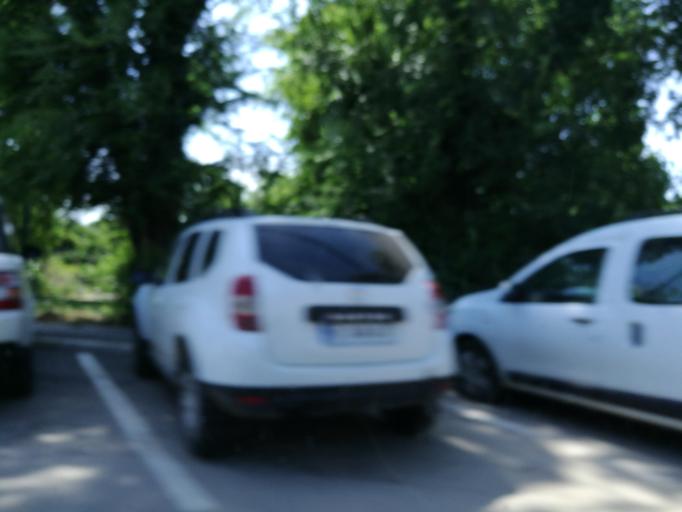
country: RO
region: Constanta
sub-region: Municipiul Constanta
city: Constanta
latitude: 44.2076
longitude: 28.6432
